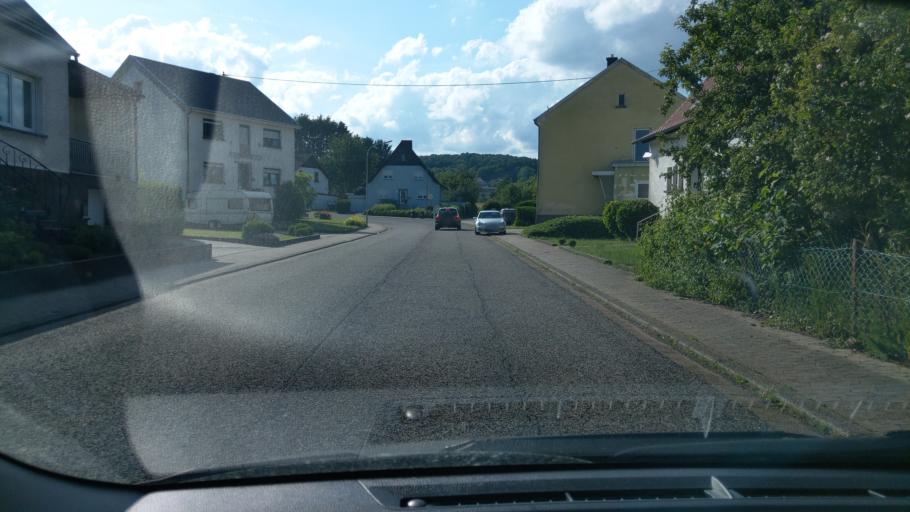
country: DE
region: Saarland
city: Tholey
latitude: 49.4951
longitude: 6.9770
